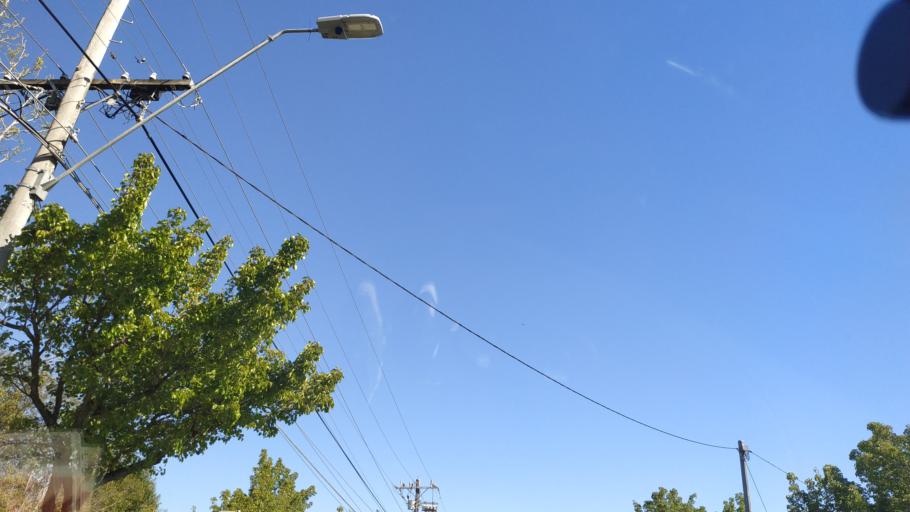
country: AU
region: Victoria
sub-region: Greater Dandenong
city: Dandenong North
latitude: -37.9792
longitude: 145.2156
